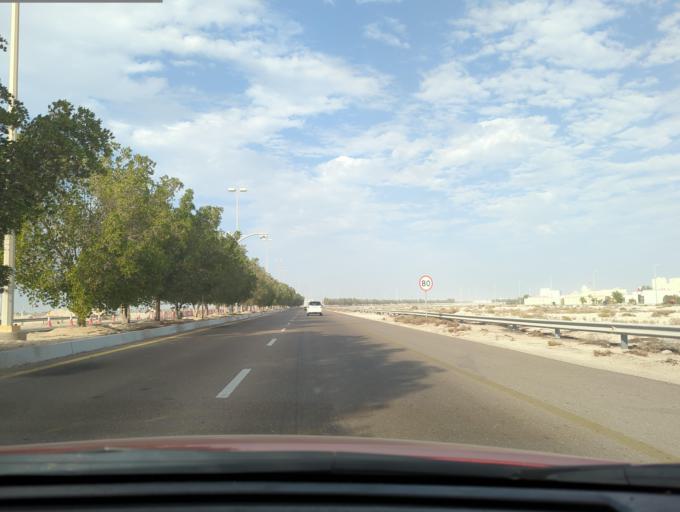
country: AE
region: Abu Dhabi
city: Abu Dhabi
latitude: 24.3913
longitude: 54.6819
